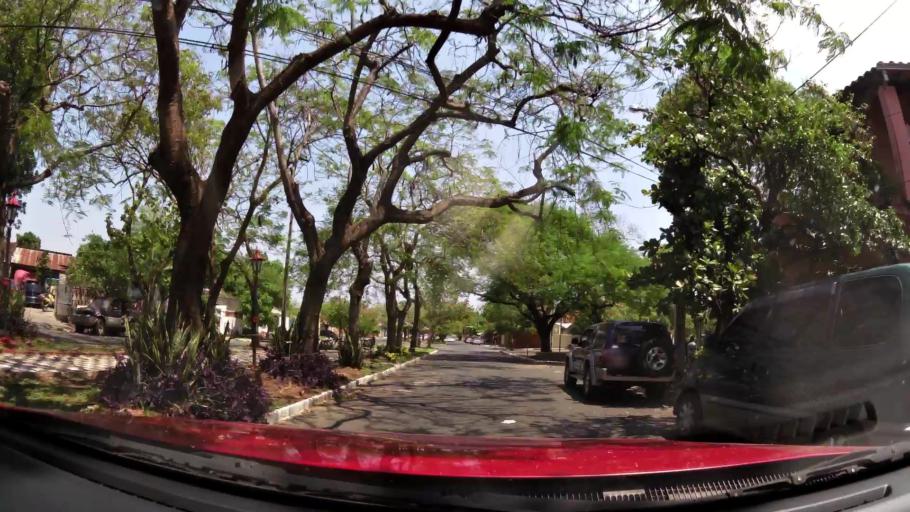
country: PY
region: Asuncion
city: Asuncion
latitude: -25.3001
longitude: -57.6505
